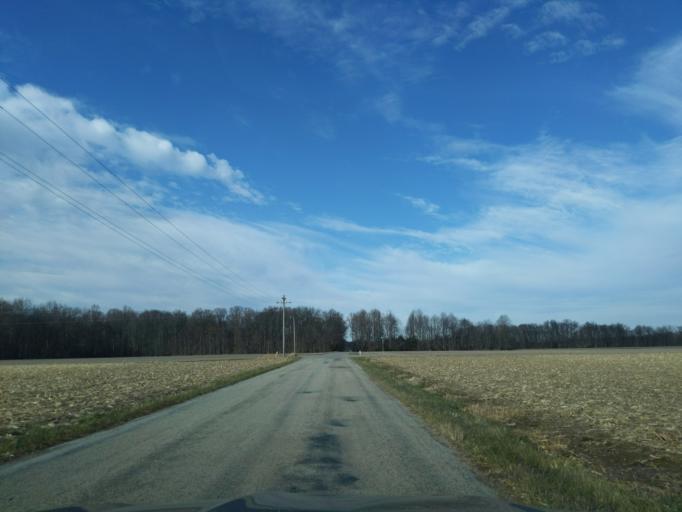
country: US
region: Indiana
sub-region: Decatur County
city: Greensburg
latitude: 39.2775
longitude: -85.4235
